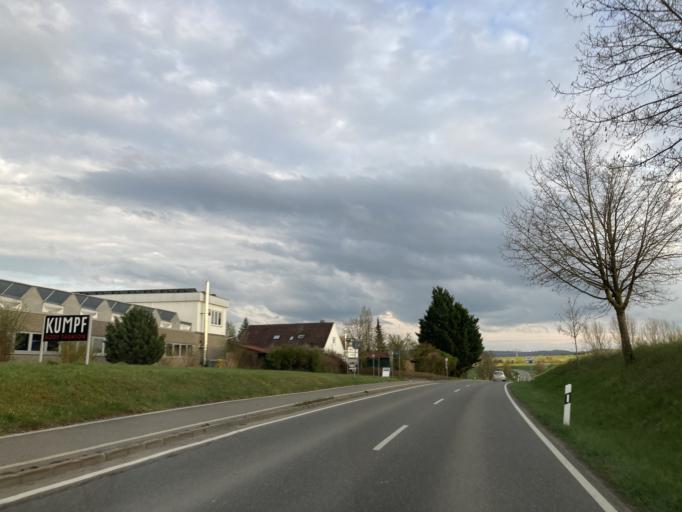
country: DE
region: Baden-Wuerttemberg
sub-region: Tuebingen Region
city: Rottenburg
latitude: 48.5038
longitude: 8.9321
